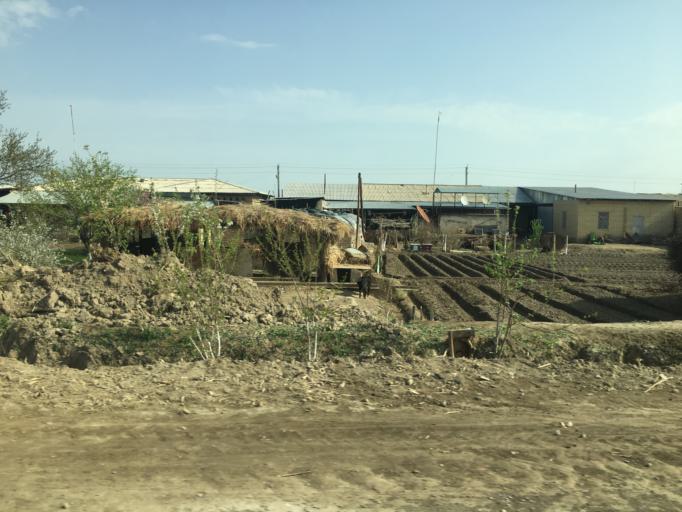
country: TM
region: Mary
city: Seydi
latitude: 39.3027
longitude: 63.0330
